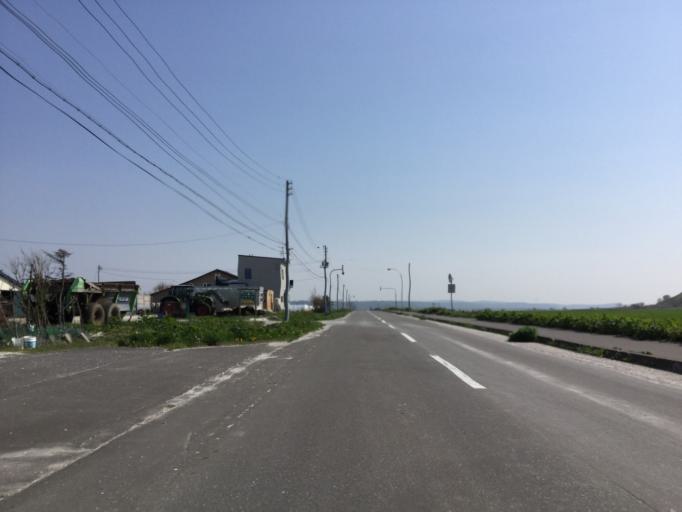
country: JP
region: Hokkaido
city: Makubetsu
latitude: 45.3985
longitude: 141.7670
